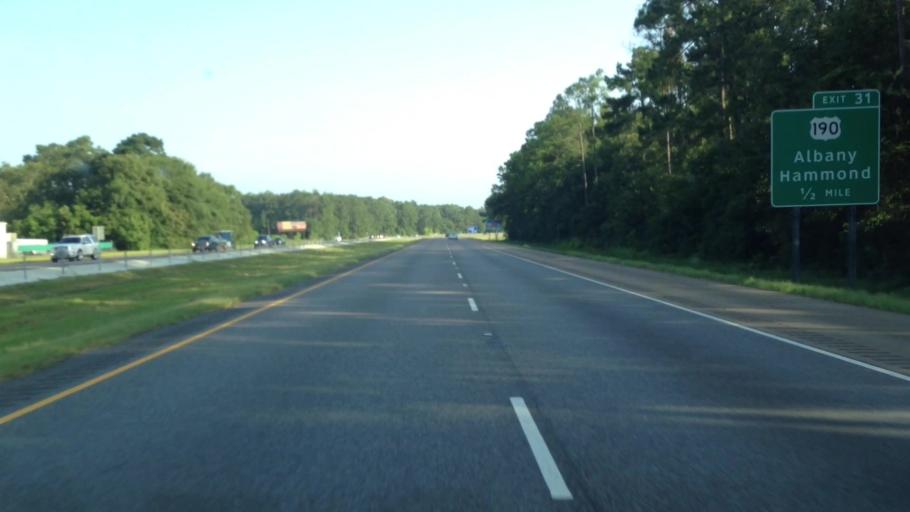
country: US
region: Louisiana
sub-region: Tangipahoa Parish
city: Hammond
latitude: 30.4946
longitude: -90.5000
